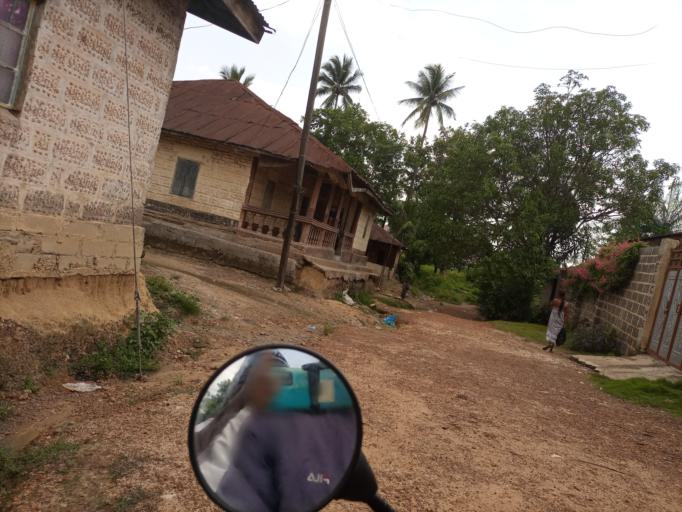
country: SL
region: Southern Province
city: Bo
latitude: 7.9566
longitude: -11.7363
